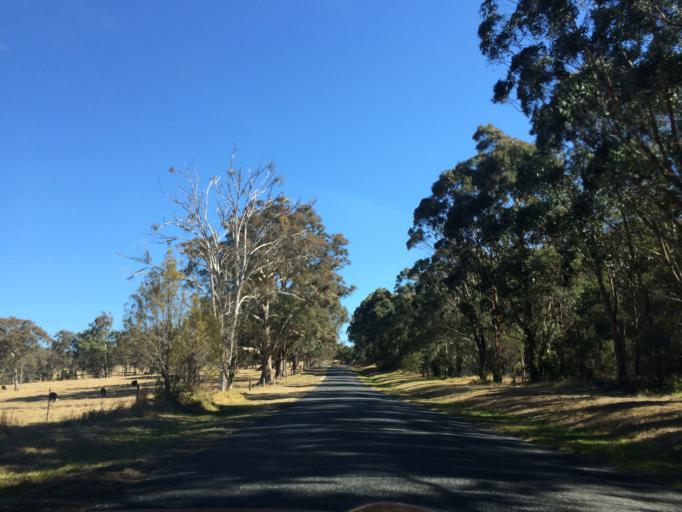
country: AU
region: Queensland
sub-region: Southern Downs
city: Stanthorpe
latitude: -28.6520
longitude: 152.0834
